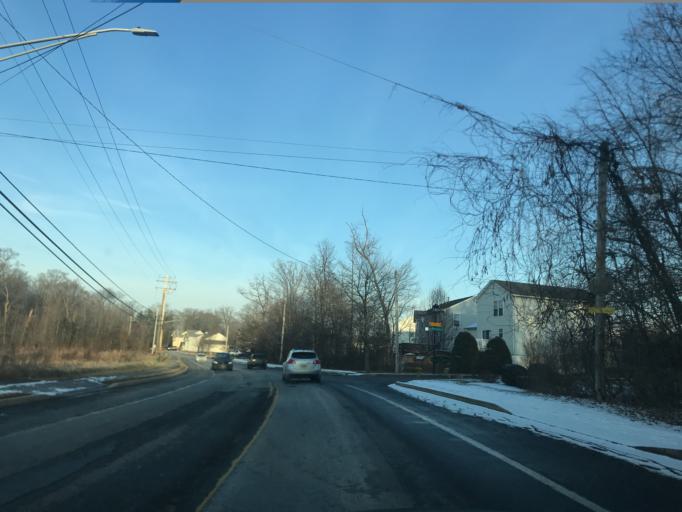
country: US
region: Maryland
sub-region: Harford County
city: Edgewood
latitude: 39.4293
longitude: -76.2803
